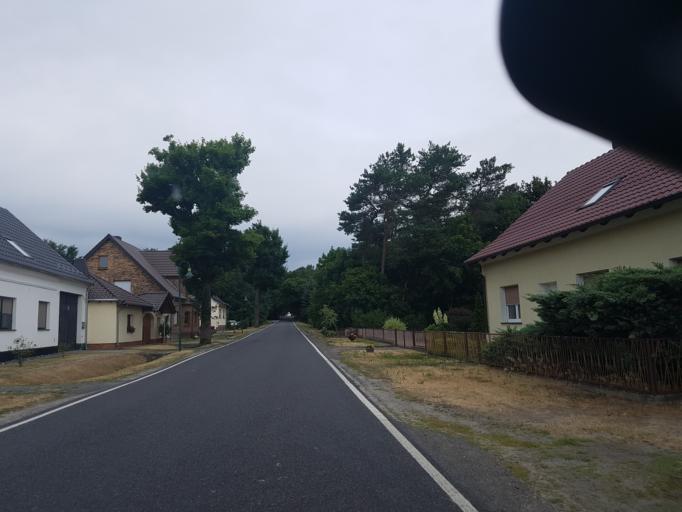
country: DE
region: Brandenburg
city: Doberlug-Kirchhain
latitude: 51.6926
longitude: 13.5098
